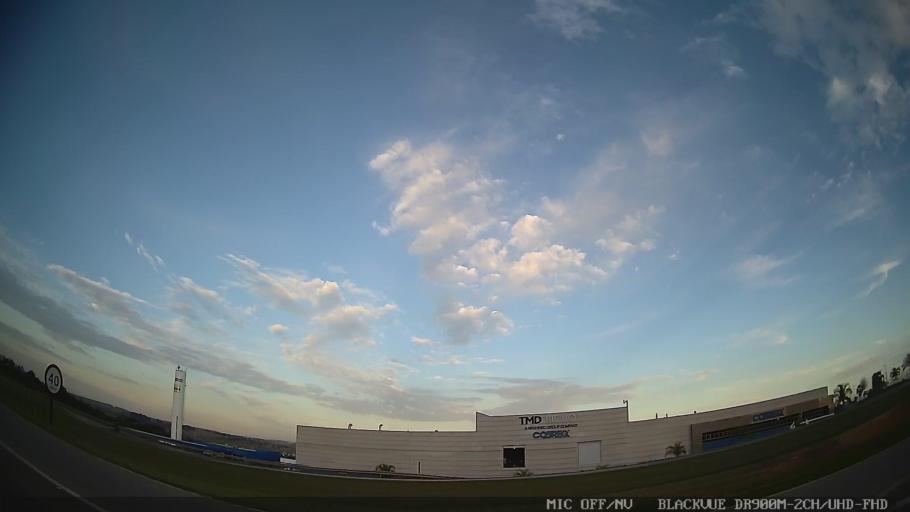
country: BR
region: Sao Paulo
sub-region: Salto
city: Salto
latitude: -23.1701
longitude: -47.2684
